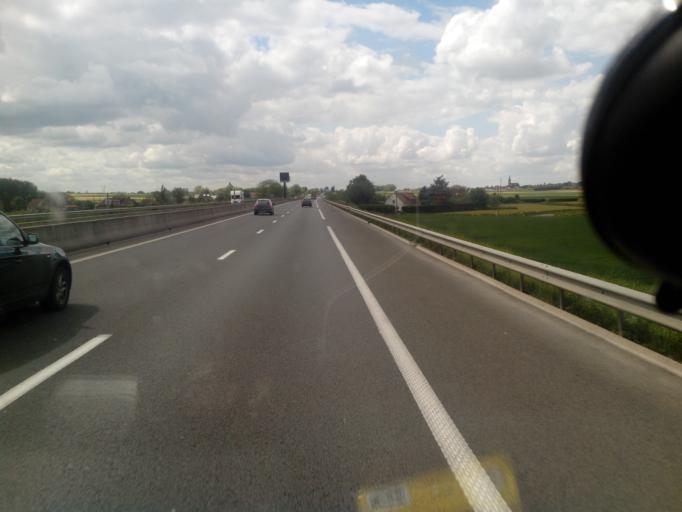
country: FR
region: Nord-Pas-de-Calais
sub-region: Departement du Nord
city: Bailleul
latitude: 50.7275
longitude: 2.7186
